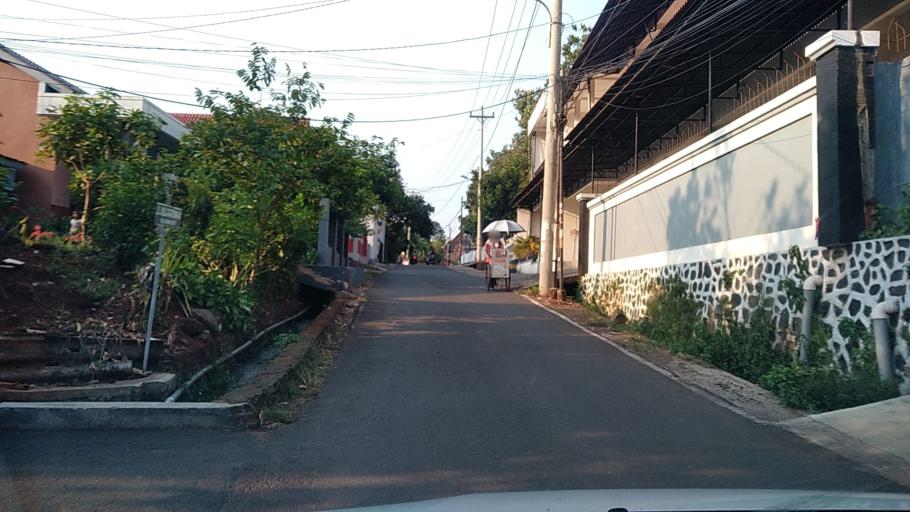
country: ID
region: Central Java
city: Semarang
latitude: -7.0685
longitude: 110.4396
